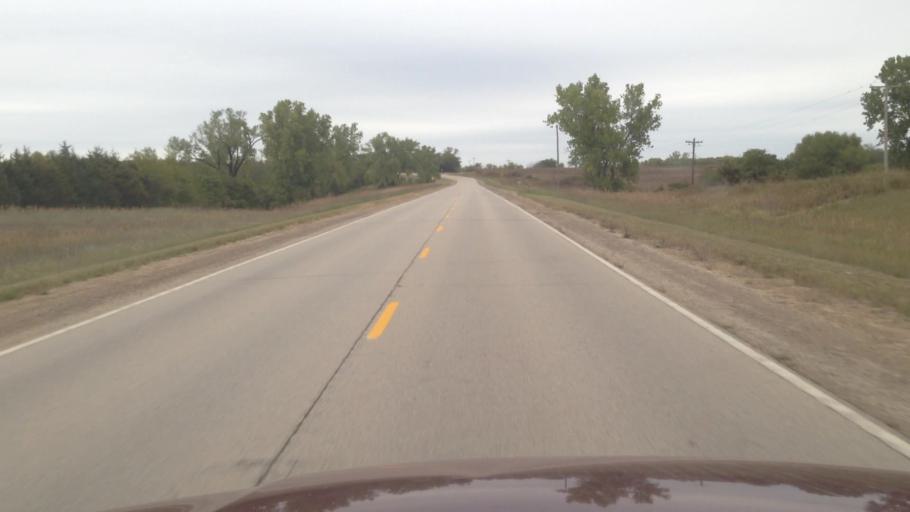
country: US
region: Kansas
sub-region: Jefferson County
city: Oskaloosa
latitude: 39.1222
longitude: -95.4836
